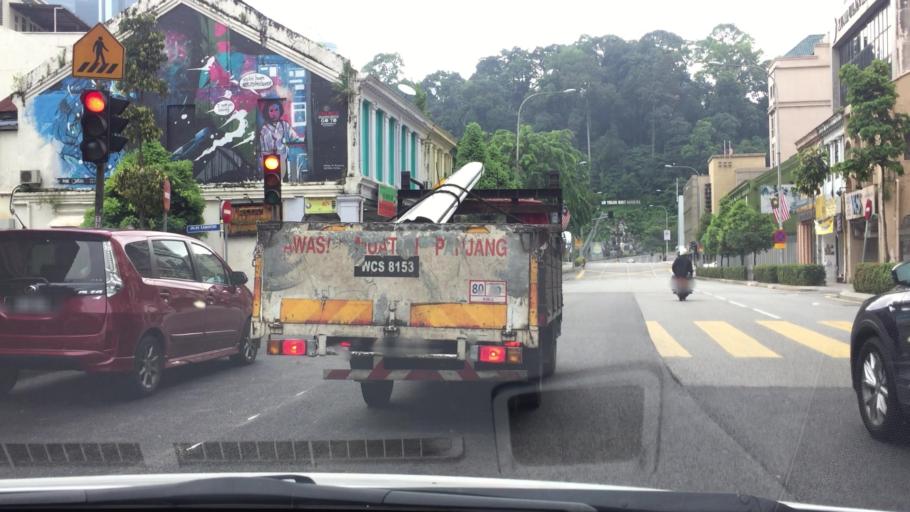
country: MY
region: Kuala Lumpur
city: Kuala Lumpur
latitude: 3.1563
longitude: 101.6998
